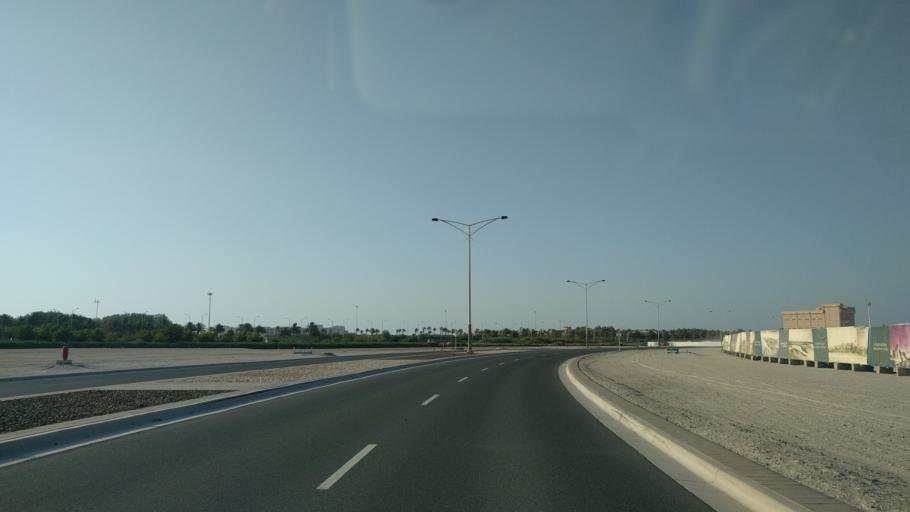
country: AE
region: Abu Dhabi
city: Abu Dhabi
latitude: 24.5356
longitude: 54.4383
